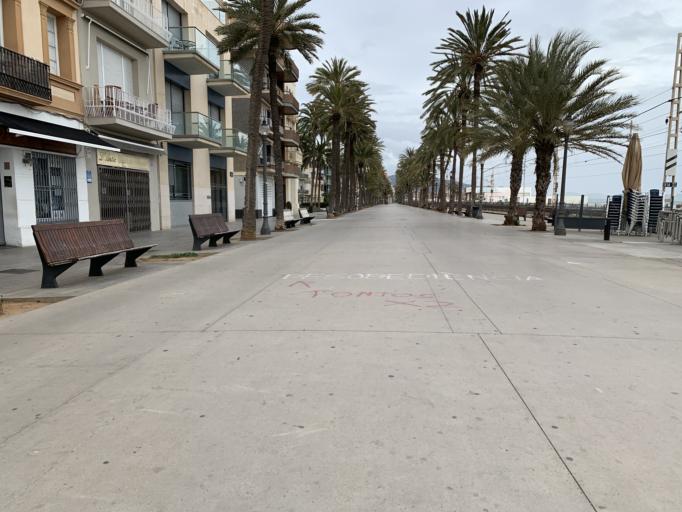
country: ES
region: Catalonia
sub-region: Provincia de Barcelona
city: Badalona
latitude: 41.4482
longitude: 2.2515
